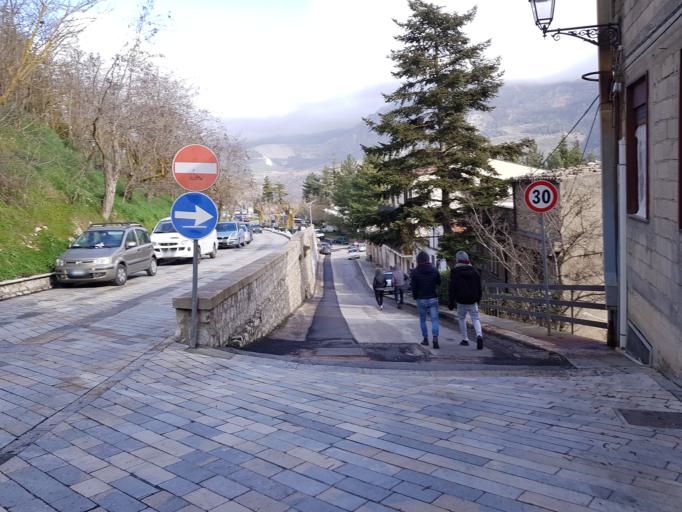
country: IT
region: Sicily
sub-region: Palermo
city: Polizzi Generosa
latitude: 37.8116
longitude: 14.0034
